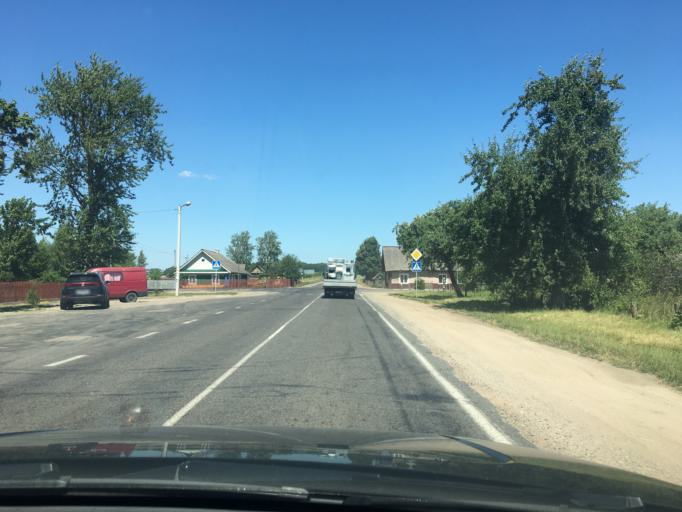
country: BY
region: Grodnenskaya
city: Iwye
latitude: 54.0645
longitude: 25.9111
